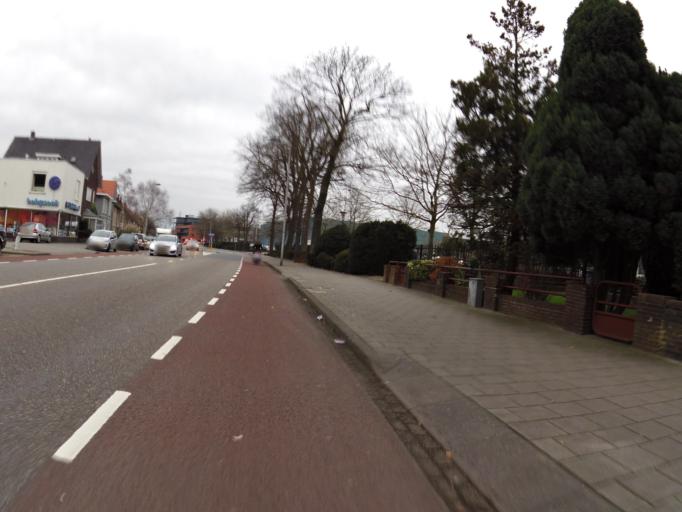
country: NL
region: North Brabant
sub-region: Gemeente Oss
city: Oss
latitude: 51.7613
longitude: 5.5306
